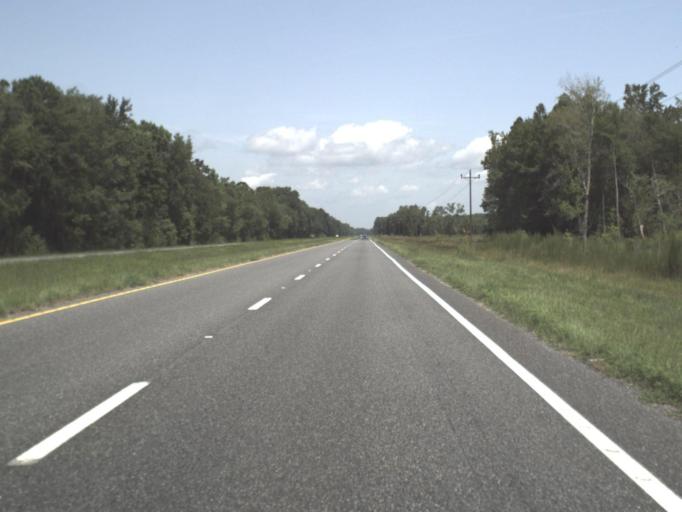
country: US
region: Florida
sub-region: Taylor County
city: Steinhatchee
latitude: 29.9044
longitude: -83.4253
